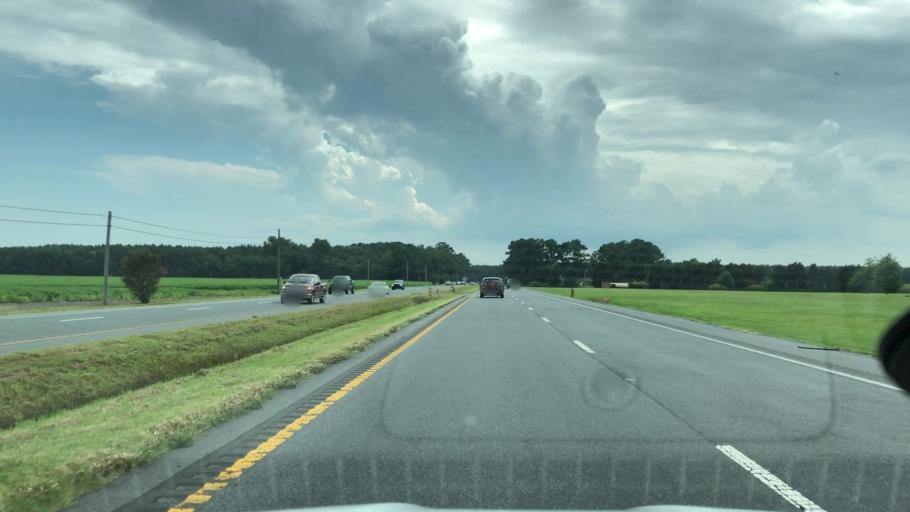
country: US
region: Virginia
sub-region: Accomack County
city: Wattsville
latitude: 37.8846
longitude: -75.5544
